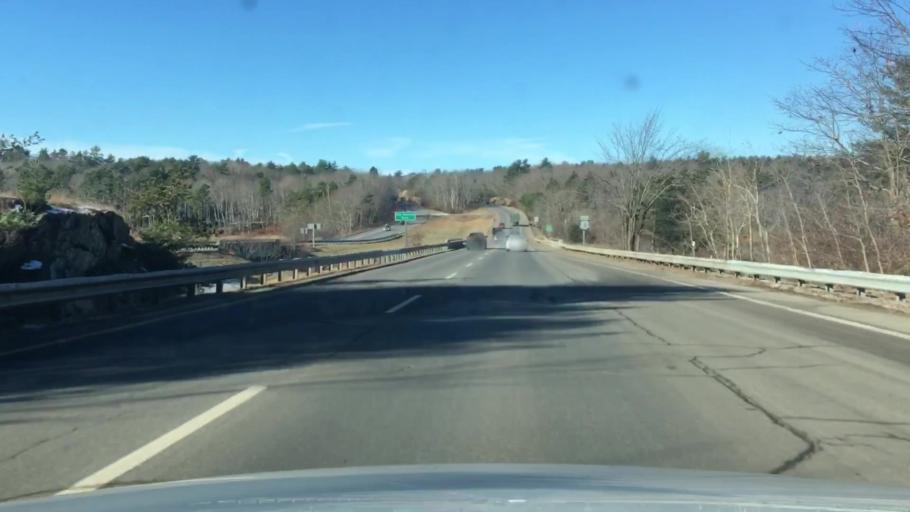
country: US
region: Maine
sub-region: Sagadahoc County
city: Bath
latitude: 43.9181
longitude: -69.8639
